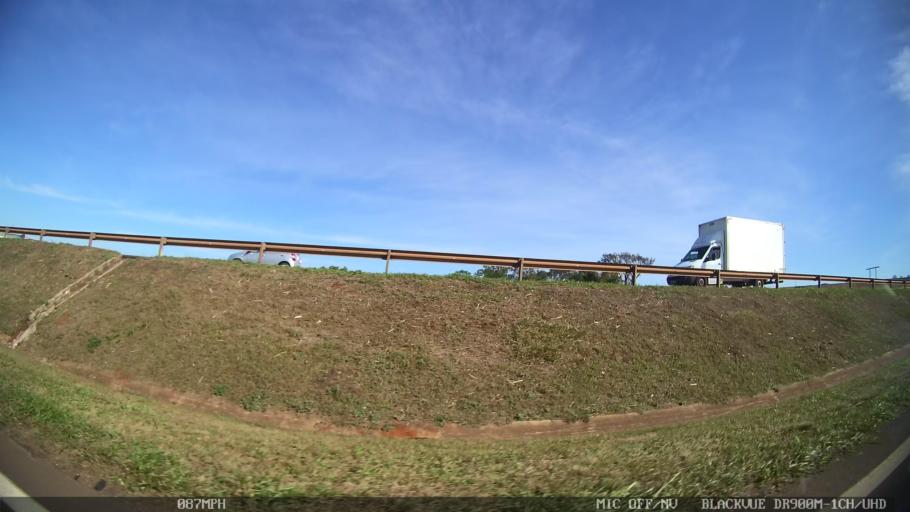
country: BR
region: Sao Paulo
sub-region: Leme
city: Leme
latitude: -22.1692
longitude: -47.3992
